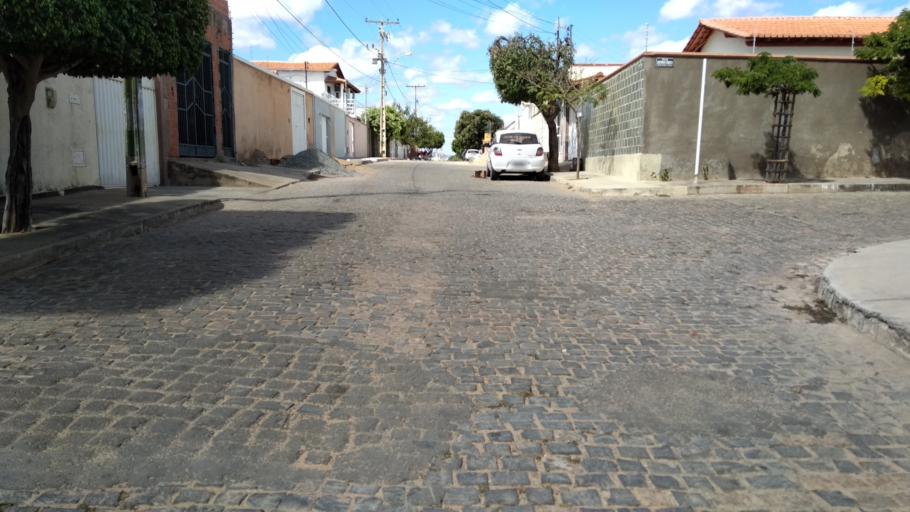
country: BR
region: Bahia
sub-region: Guanambi
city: Guanambi
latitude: -14.2347
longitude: -42.7745
